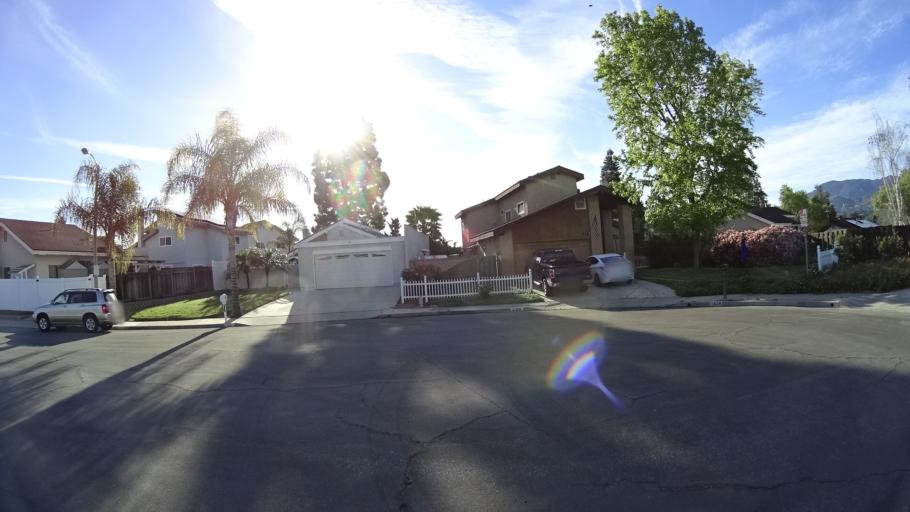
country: US
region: California
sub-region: Ventura County
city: Casa Conejo
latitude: 34.1872
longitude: -118.9518
